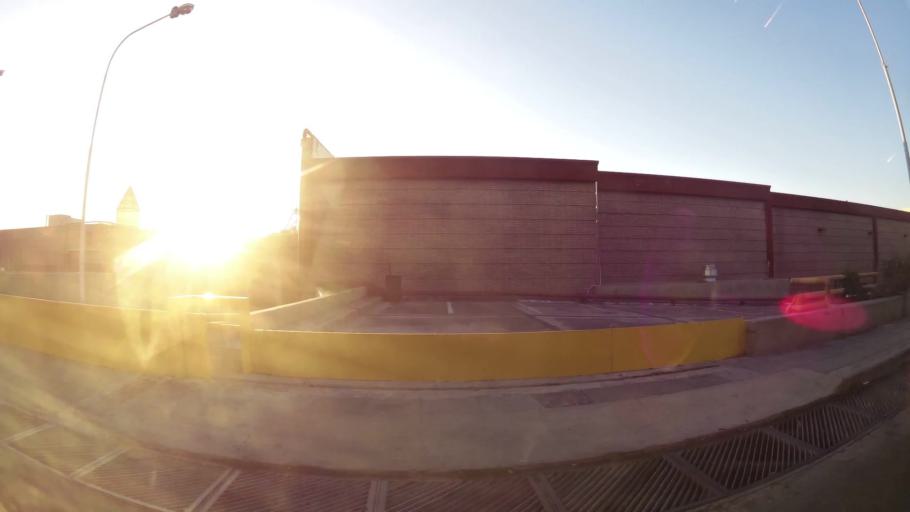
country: AR
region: Cordoba
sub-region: Departamento de Capital
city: Cordoba
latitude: -31.3807
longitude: -64.2134
